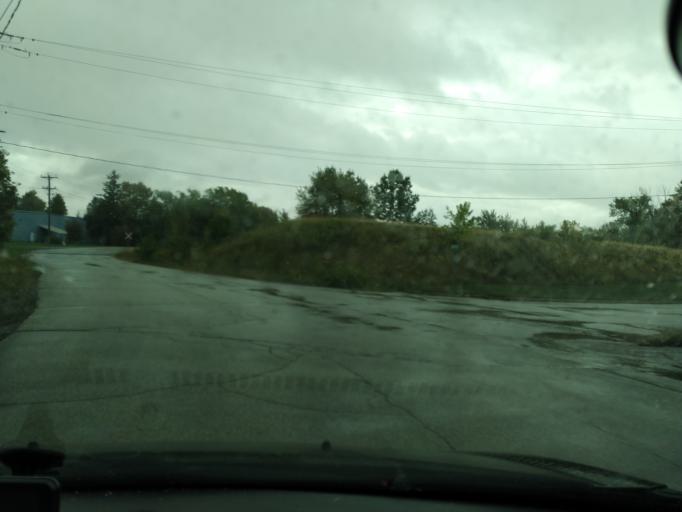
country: CA
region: Ontario
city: Barrie
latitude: 44.3573
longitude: -79.6691
